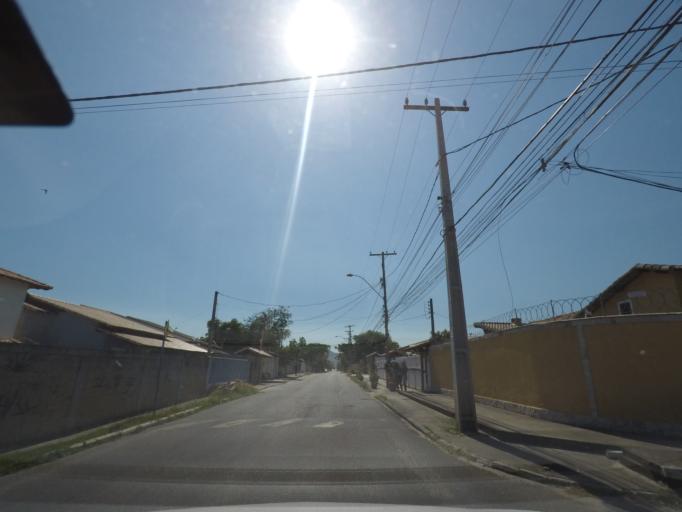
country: BR
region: Rio de Janeiro
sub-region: Marica
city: Marica
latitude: -22.9671
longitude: -42.9473
